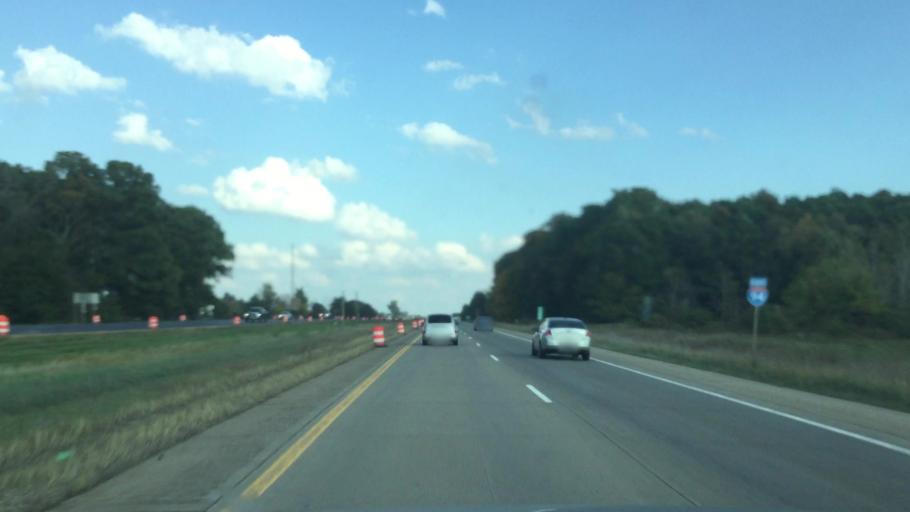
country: US
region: Michigan
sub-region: Calhoun County
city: Marshall
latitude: 42.2825
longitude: -84.9184
